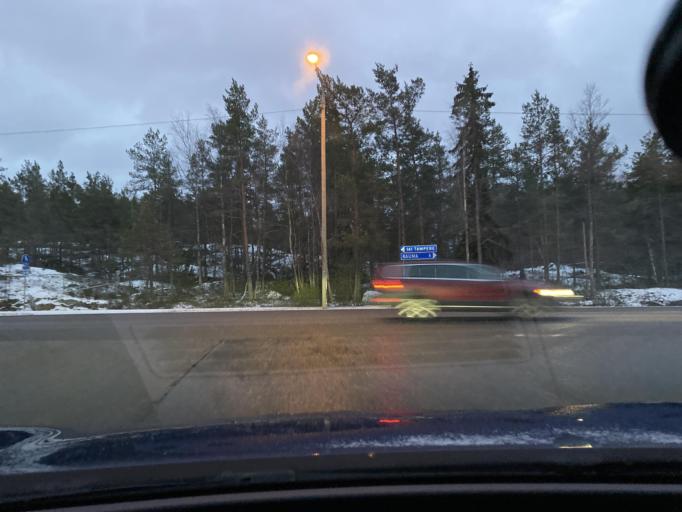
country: FI
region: Satakunta
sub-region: Rauma
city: Rauma
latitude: 61.1361
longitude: 21.5779
